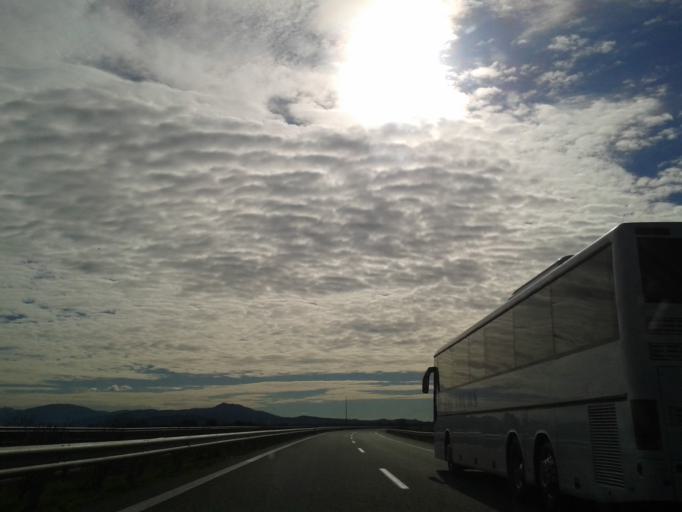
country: GR
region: West Greece
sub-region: Nomos Aitolias kai Akarnanias
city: Lepenou
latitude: 38.6576
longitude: 21.2433
